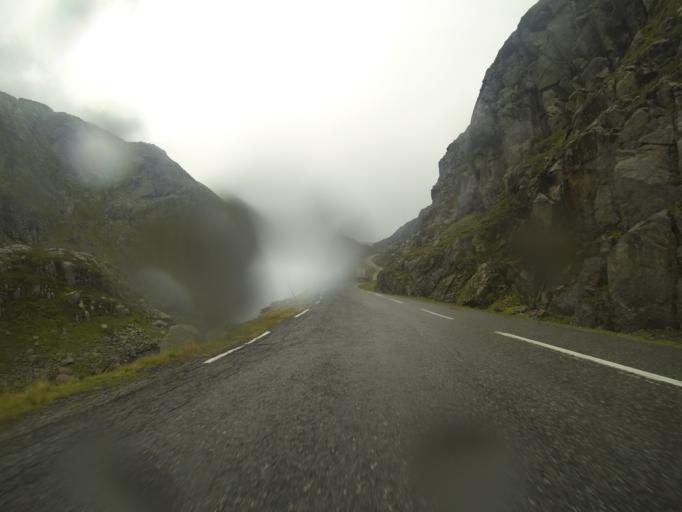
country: NO
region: Hordaland
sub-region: Odda
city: Odda
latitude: 59.7672
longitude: 6.7334
